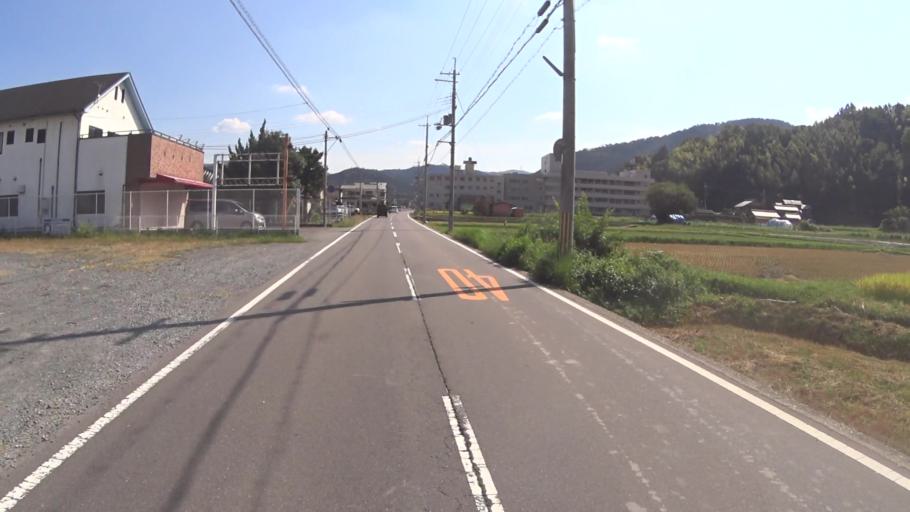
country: JP
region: Kyoto
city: Kameoka
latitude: 35.0041
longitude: 135.5777
